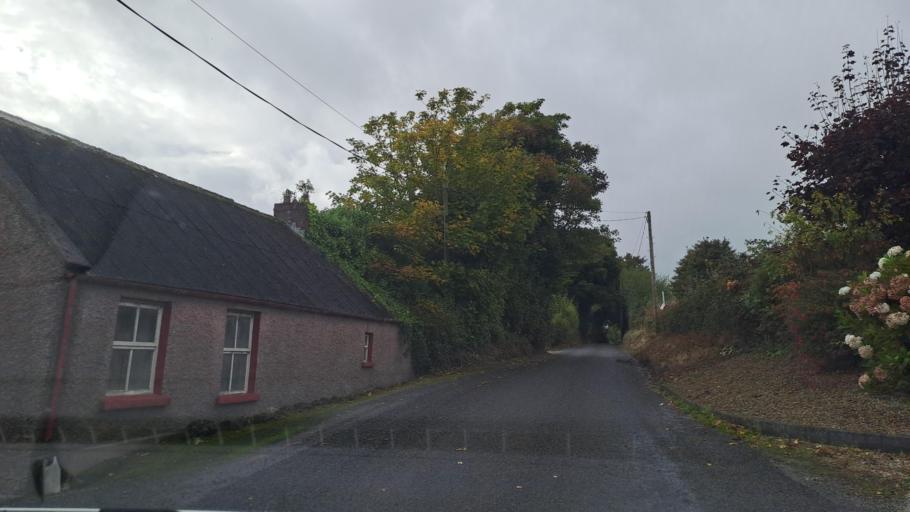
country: IE
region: Ulster
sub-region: County Monaghan
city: Carrickmacross
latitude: 53.9673
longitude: -6.7632
